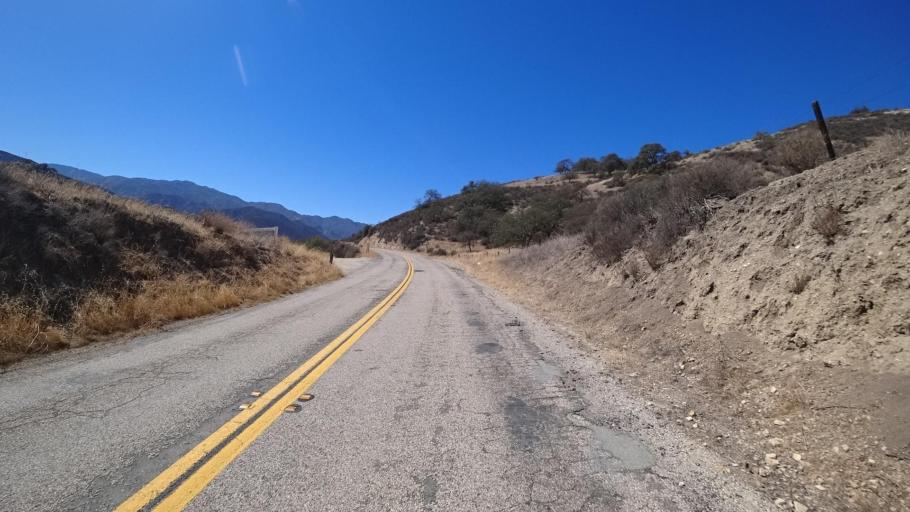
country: US
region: California
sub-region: Monterey County
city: Greenfield
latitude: 36.2707
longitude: -121.4033
